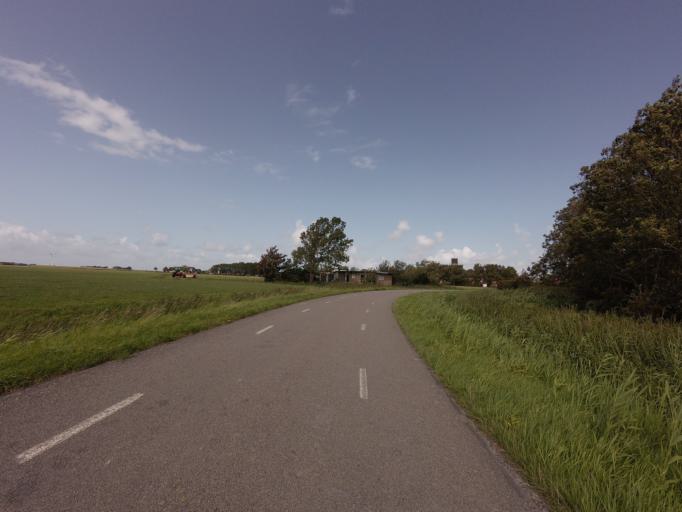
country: NL
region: Friesland
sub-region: Gemeente Harlingen
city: Harlingen
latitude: 53.1124
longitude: 5.4402
